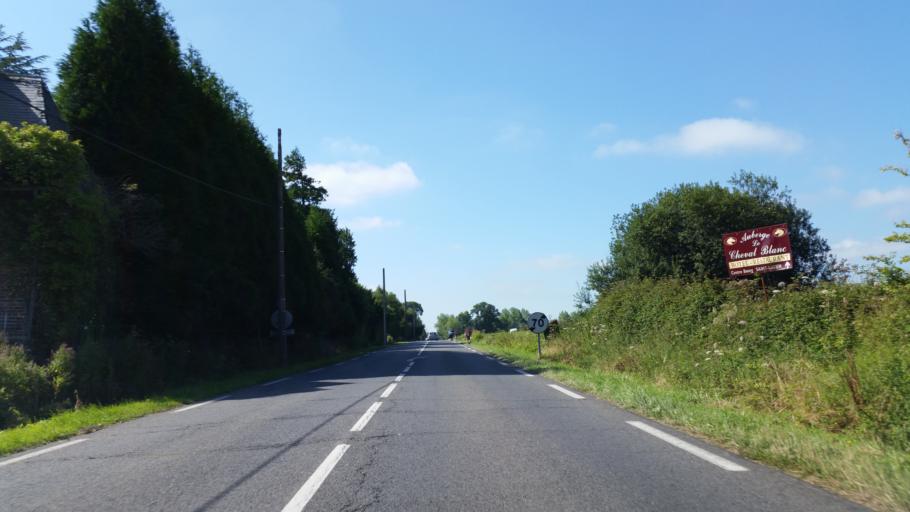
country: FR
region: Lower Normandy
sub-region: Departement du Calvados
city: Saint-Gatien-des-Bois
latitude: 49.3612
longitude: 0.1994
